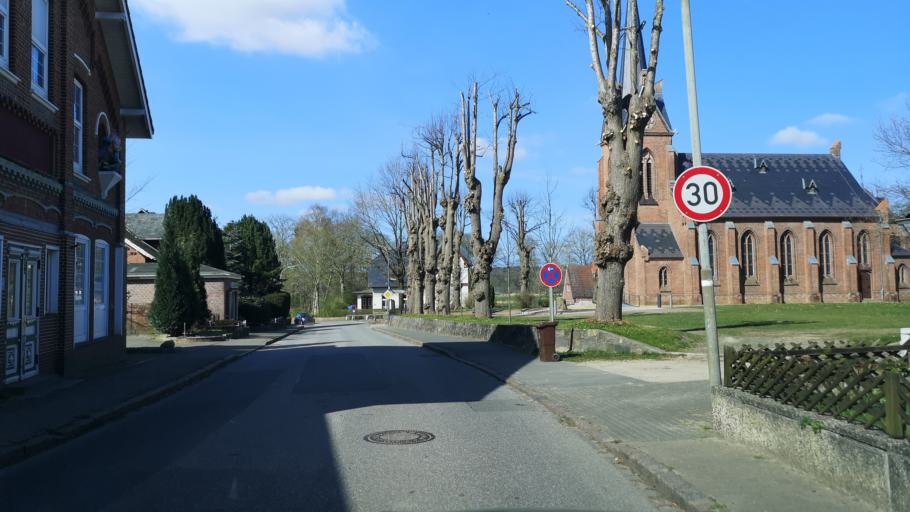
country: DE
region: Schleswig-Holstein
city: Munsterdorf
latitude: 53.9029
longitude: 9.5410
